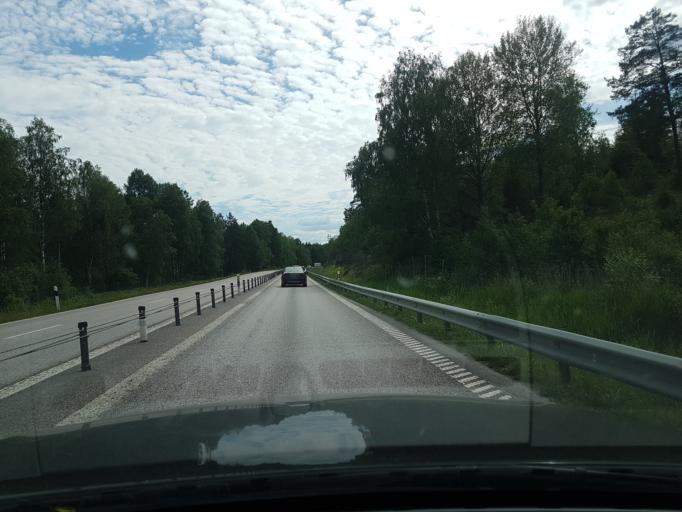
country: SE
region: Stockholm
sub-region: Vallentuna Kommun
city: Vallentuna
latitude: 59.5281
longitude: 18.1897
